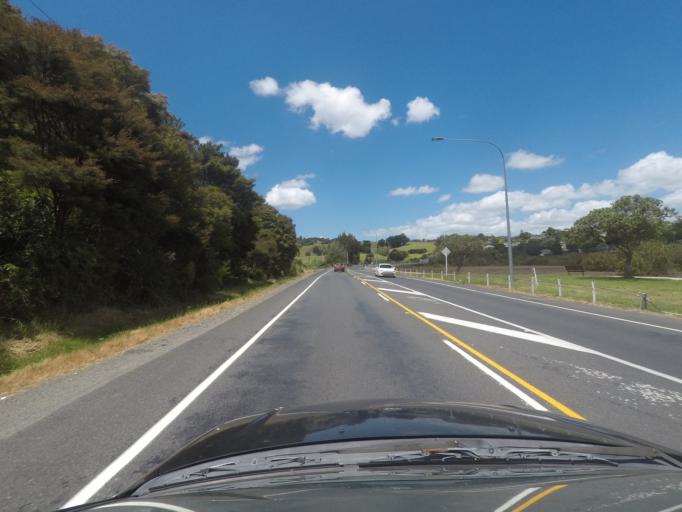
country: NZ
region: Northland
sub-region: Whangarei
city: Whangarei
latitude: -35.7387
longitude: 174.3597
